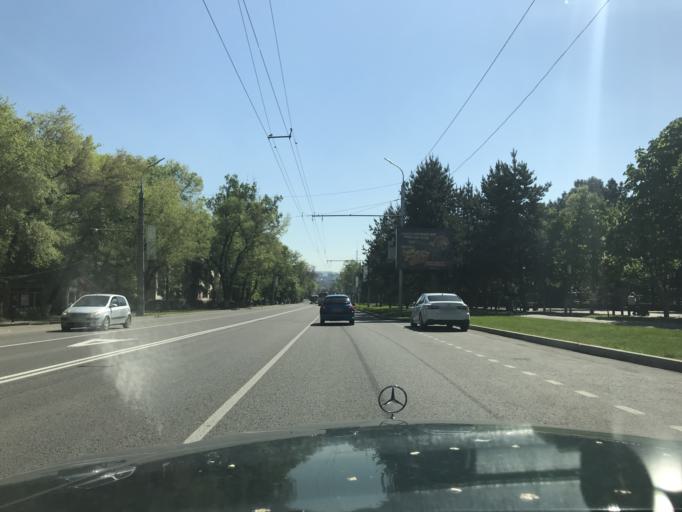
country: KZ
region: Almaty Qalasy
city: Almaty
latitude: 43.2262
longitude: 76.9111
